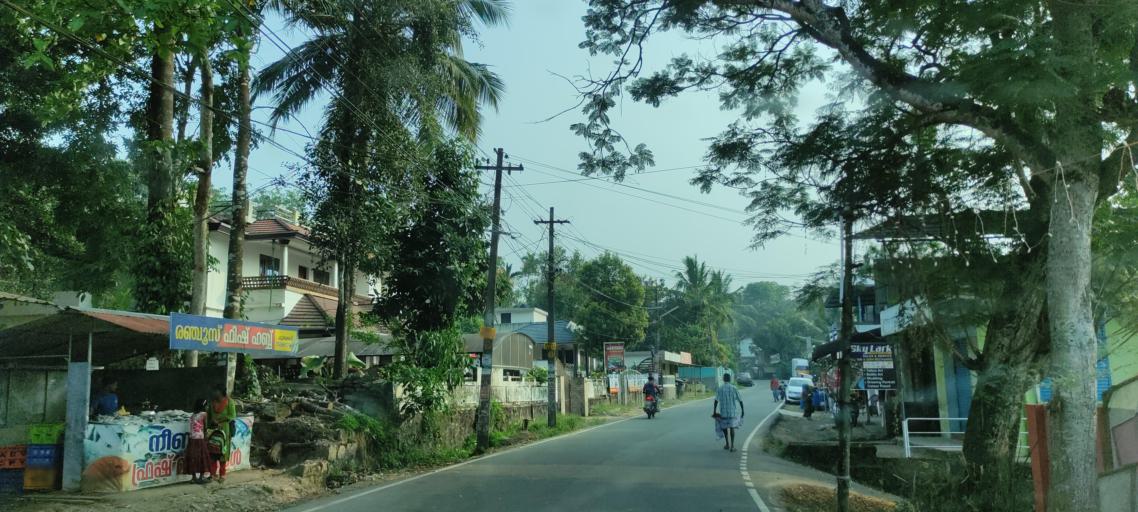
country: IN
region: Kerala
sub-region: Pattanamtitta
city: Adur
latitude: 9.1179
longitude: 76.7315
